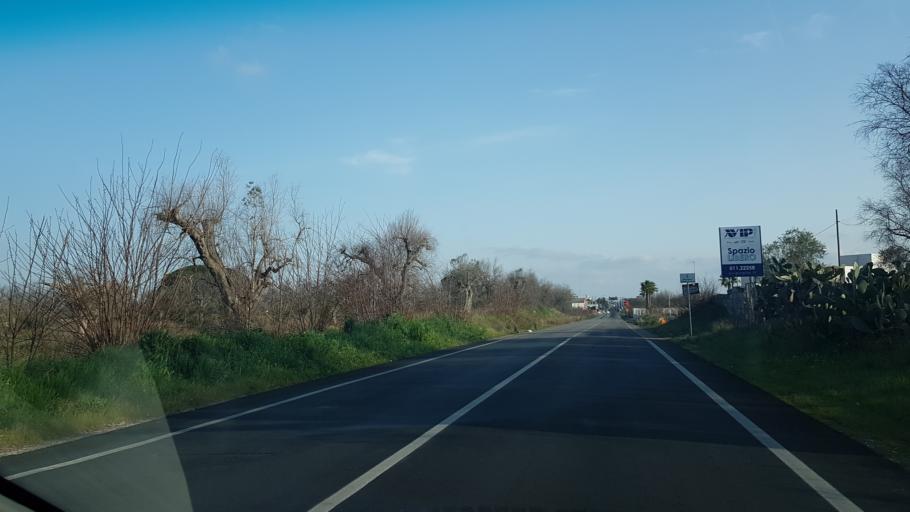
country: IT
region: Apulia
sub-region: Provincia di Lecce
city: Trepuzzi
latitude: 40.4150
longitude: 18.0630
